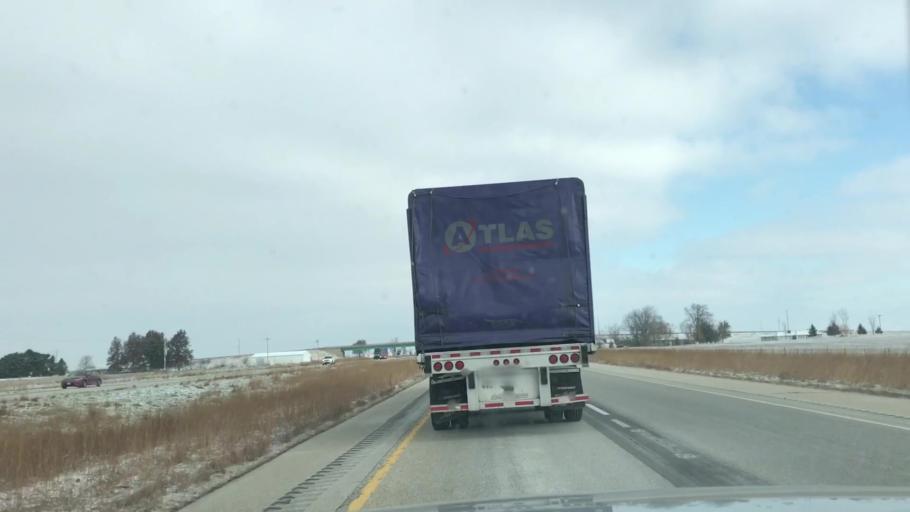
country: US
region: Illinois
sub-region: Sangamon County
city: Divernon
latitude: 39.5201
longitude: -89.6453
